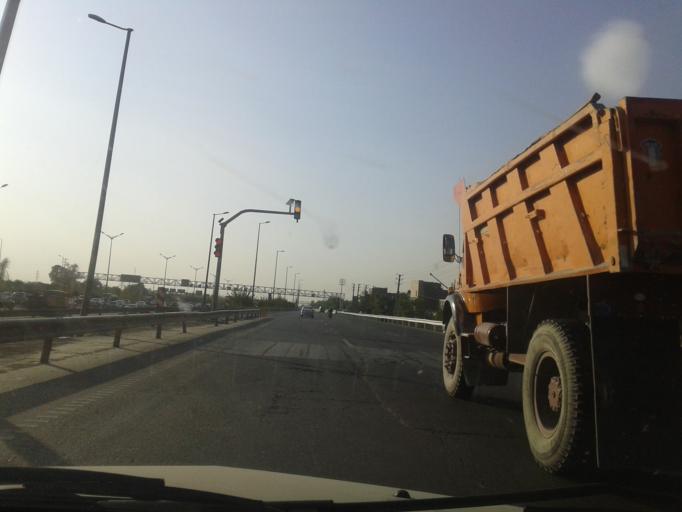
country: IR
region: Tehran
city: Eslamshahr
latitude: 35.6525
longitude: 51.2688
